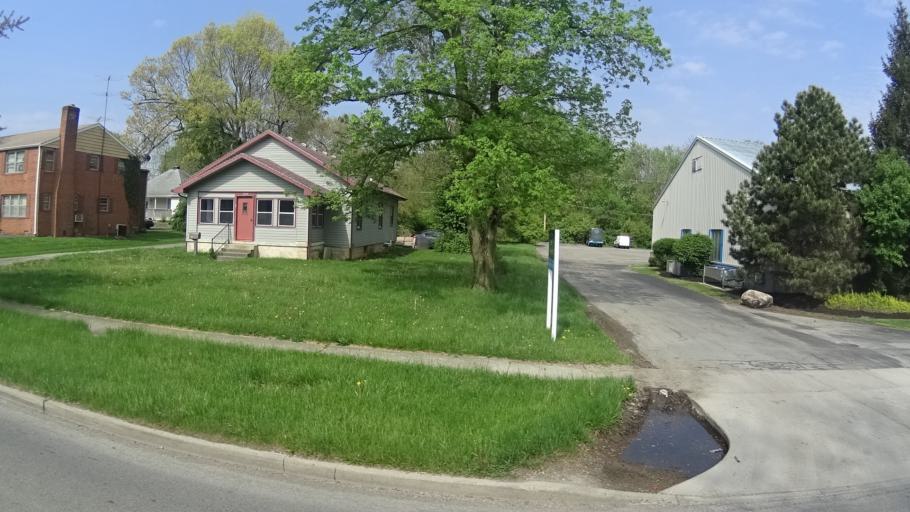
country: US
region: Indiana
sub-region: Madison County
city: Anderson
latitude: 40.1249
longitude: -85.6783
